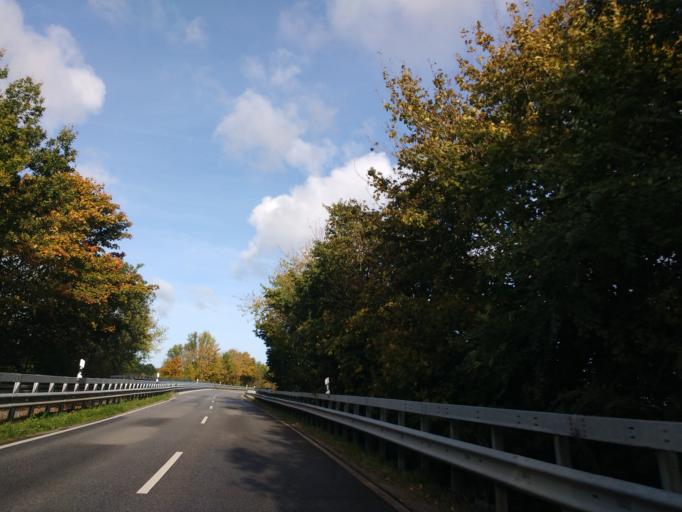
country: DE
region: Schleswig-Holstein
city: Altenkrempe
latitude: 54.1255
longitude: 10.8219
